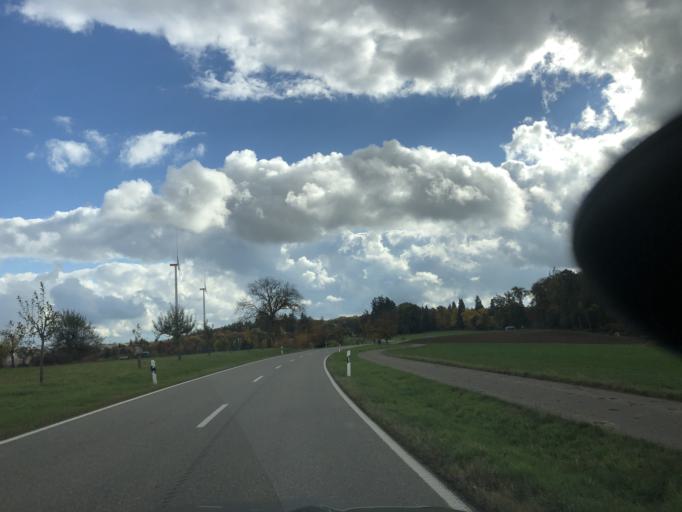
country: DE
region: Baden-Wuerttemberg
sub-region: Regierungsbezirk Stuttgart
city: Winterbach
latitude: 48.7830
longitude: 9.4540
